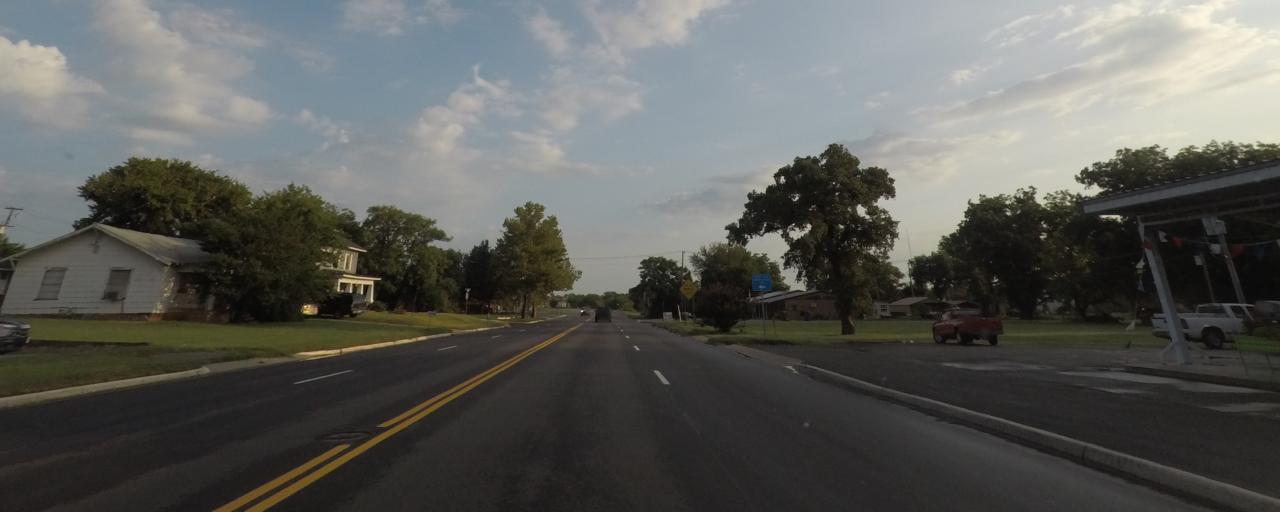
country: US
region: Oklahoma
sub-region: Stephens County
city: Comanche
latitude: 34.3713
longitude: -97.9642
